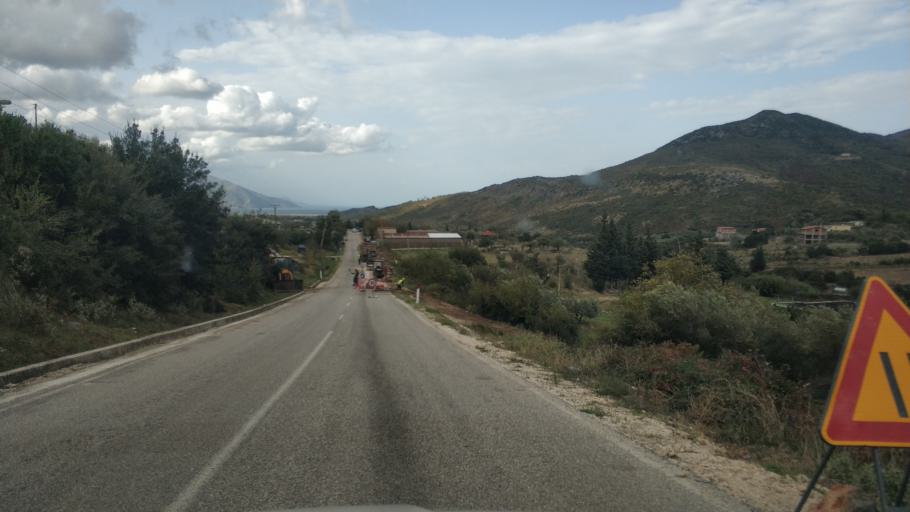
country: AL
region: Vlore
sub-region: Rrethi i Vlores
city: Orikum
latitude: 40.2685
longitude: 19.5153
